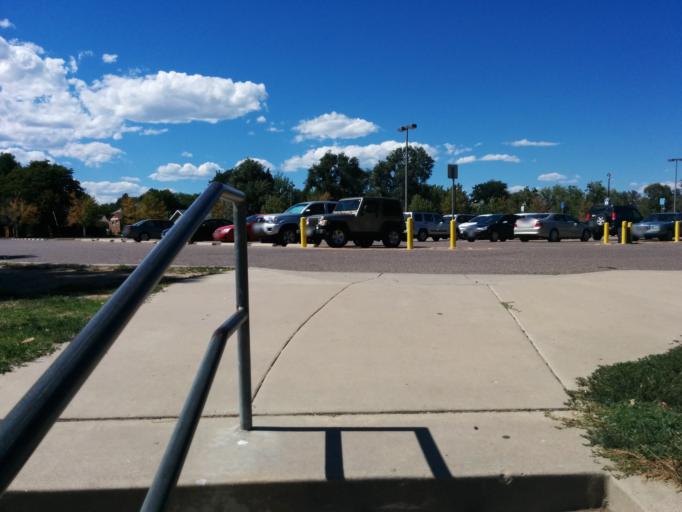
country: US
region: Colorado
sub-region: Arapahoe County
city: Glendale
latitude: 39.6911
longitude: -104.9674
